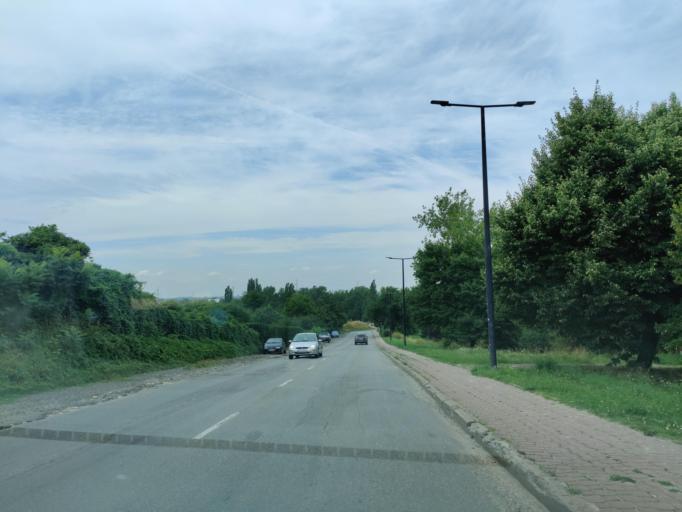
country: PL
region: Silesian Voivodeship
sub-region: Powiat bedzinski
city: Bedzin
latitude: 50.2885
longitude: 19.1625
